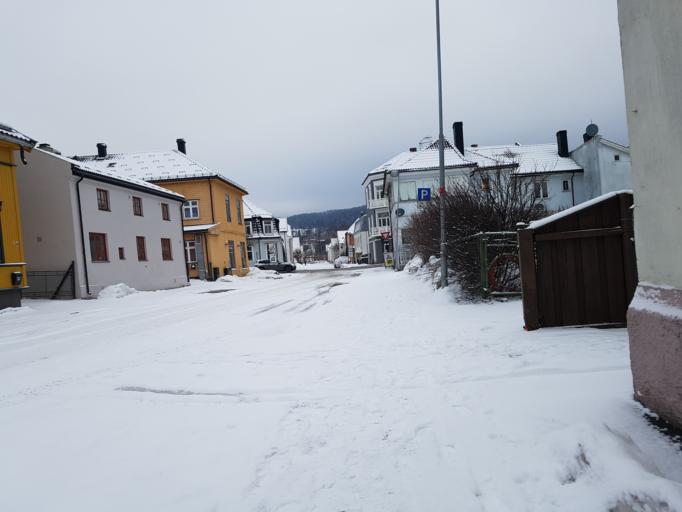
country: NO
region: Buskerud
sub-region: Drammen
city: Drammen
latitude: 59.7378
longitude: 10.1931
